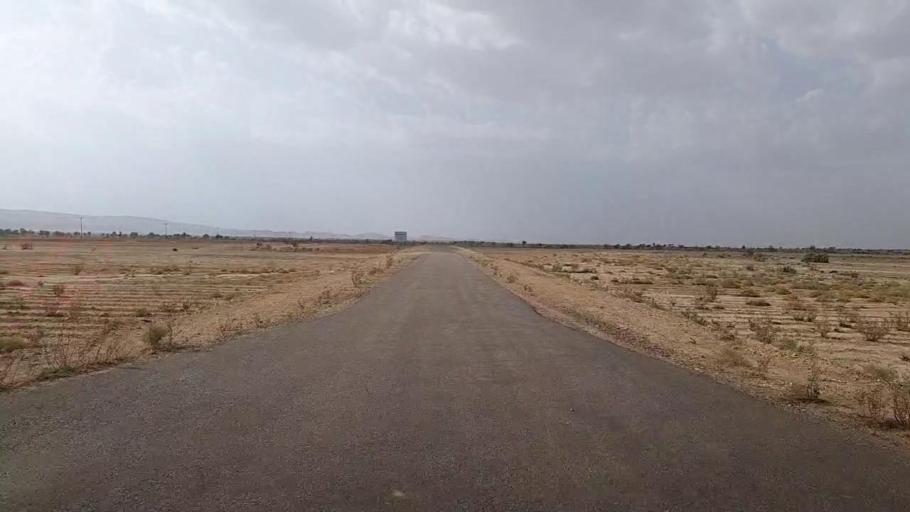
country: PK
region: Sindh
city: Jamshoro
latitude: 25.4440
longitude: 67.6816
